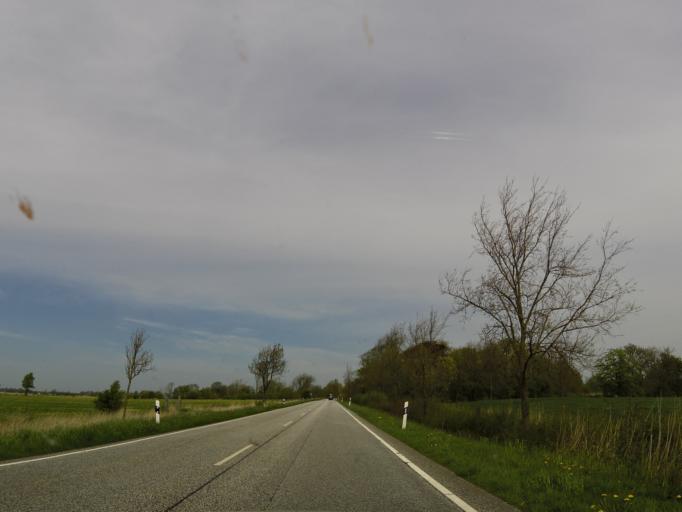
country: DE
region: Schleswig-Holstein
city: Oldenswort
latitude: 54.3500
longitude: 8.9709
